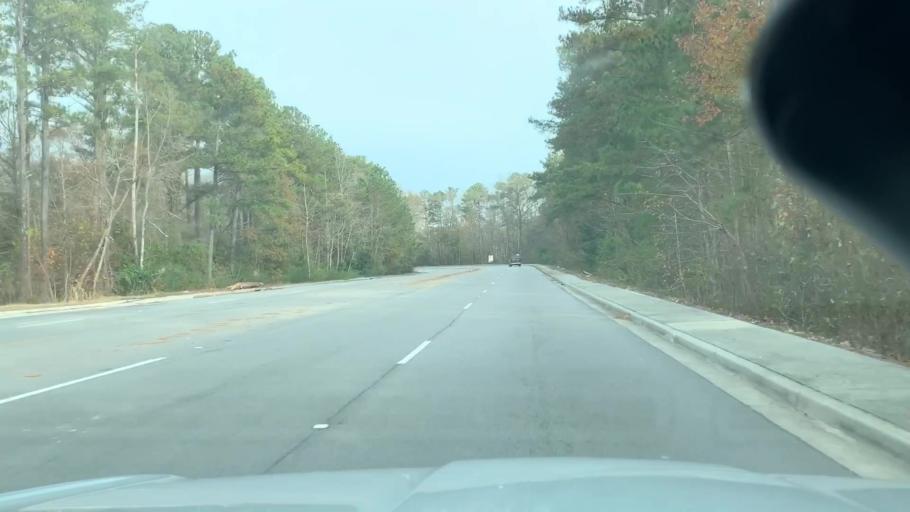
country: US
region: South Carolina
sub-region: Richland County
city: Dentsville
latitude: 34.0651
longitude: -80.9474
